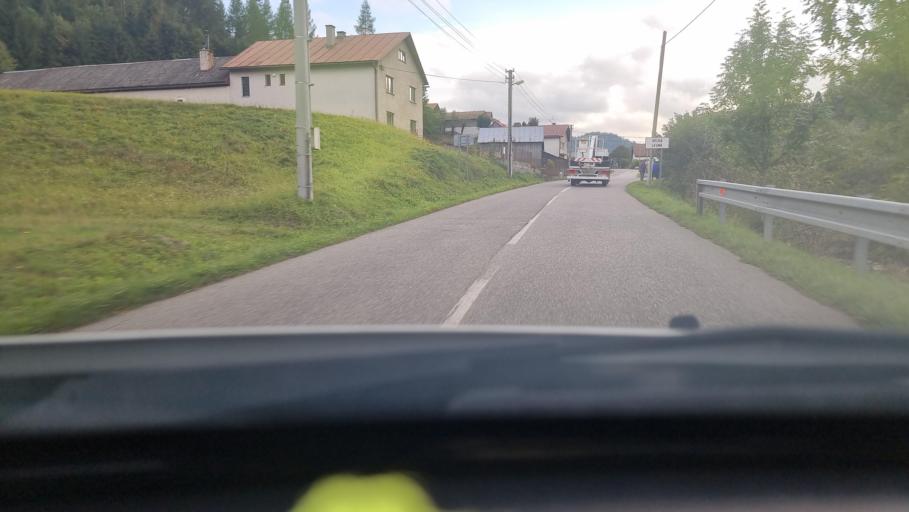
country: PL
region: Lesser Poland Voivodeship
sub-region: Powiat nowotarski
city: Szczawnica
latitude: 49.3507
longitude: 20.4423
